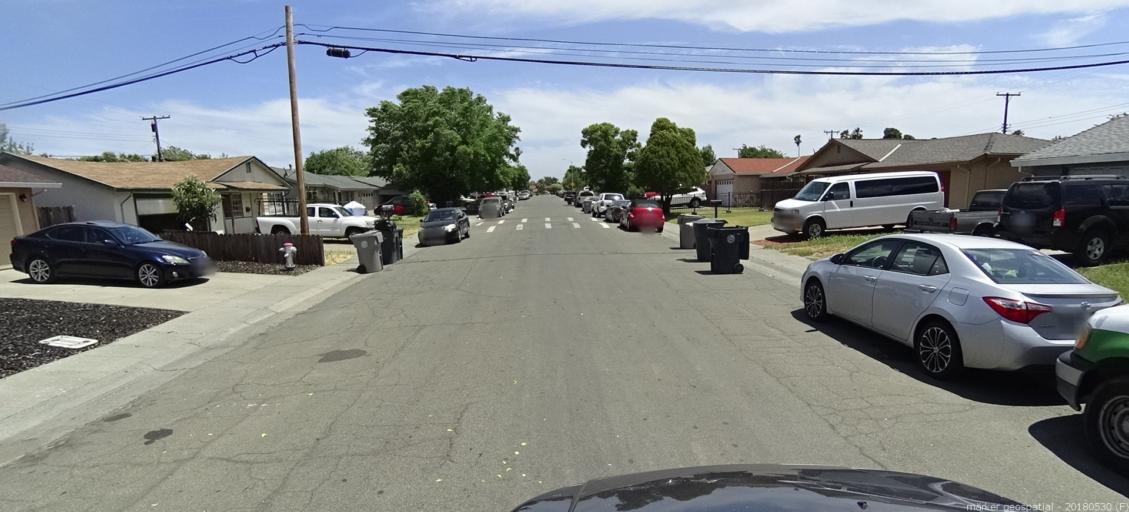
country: US
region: California
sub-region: Sacramento County
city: Sacramento
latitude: 38.6253
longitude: -121.4652
